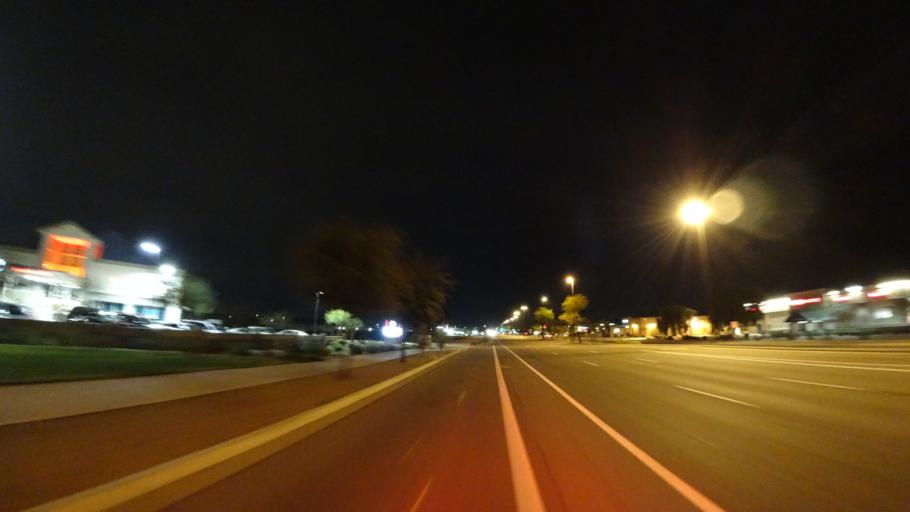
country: US
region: Arizona
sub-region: Maricopa County
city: Queen Creek
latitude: 33.2787
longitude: -111.6864
